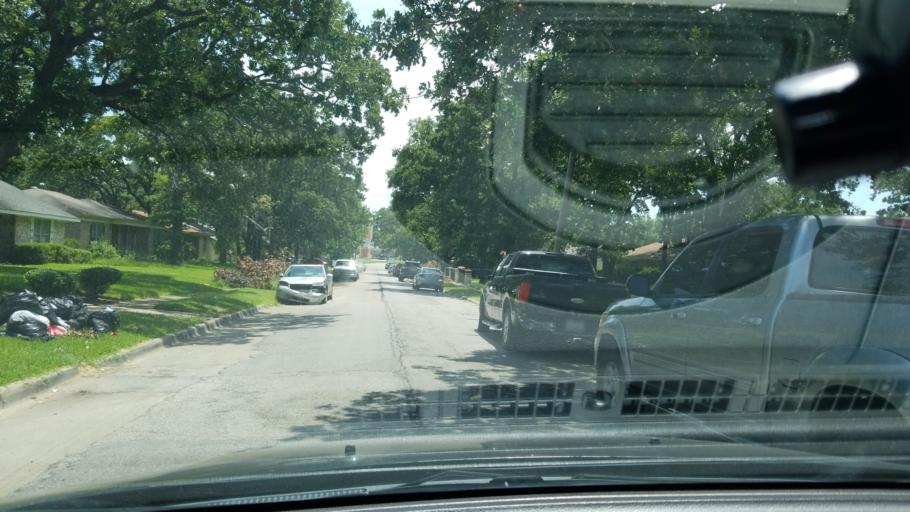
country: US
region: Texas
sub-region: Dallas County
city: Balch Springs
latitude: 32.7408
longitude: -96.6447
